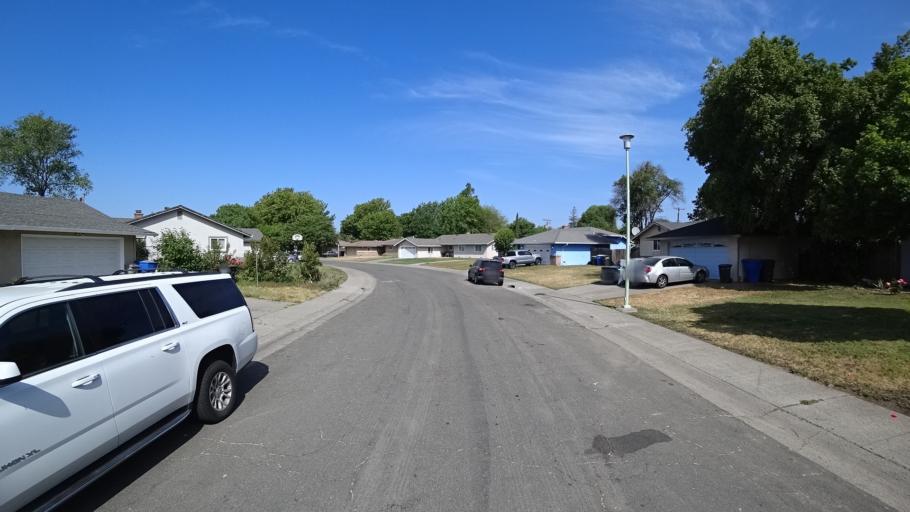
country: US
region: California
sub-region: Sacramento County
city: Parkway
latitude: 38.4971
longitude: -121.4900
